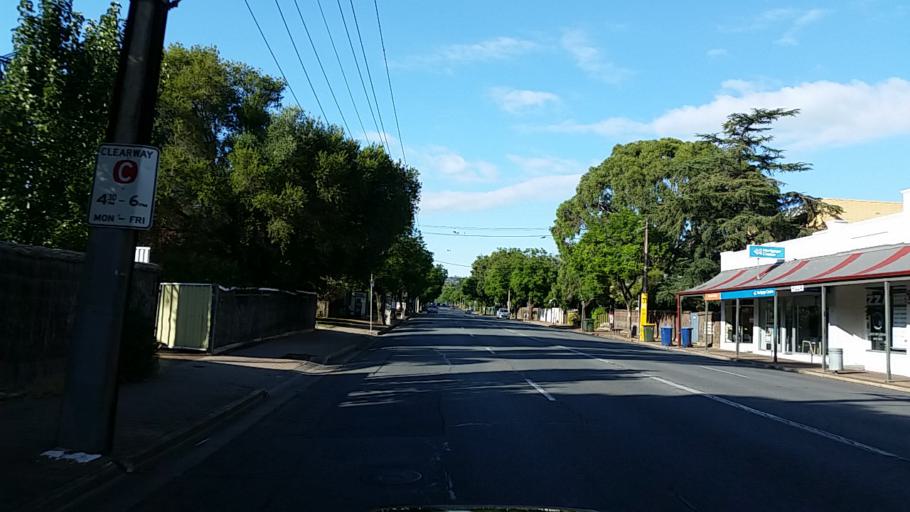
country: AU
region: South Australia
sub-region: Unley
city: Fullarton
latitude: -34.9509
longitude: 138.6254
